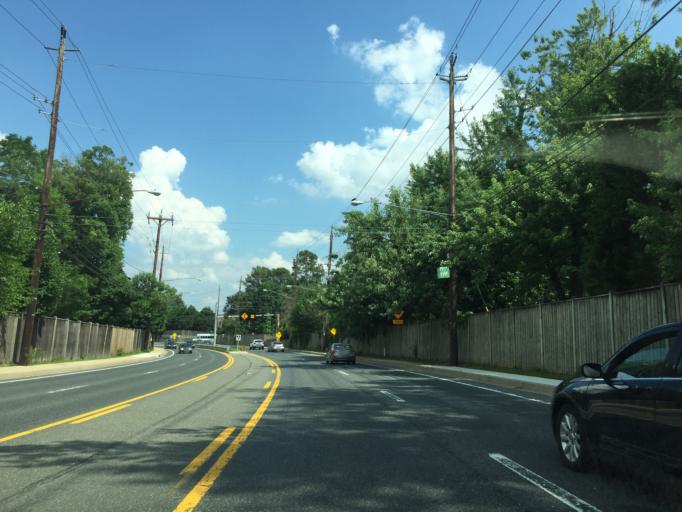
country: US
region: Maryland
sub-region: Montgomery County
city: Colesville
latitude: 39.0670
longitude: -76.9848
